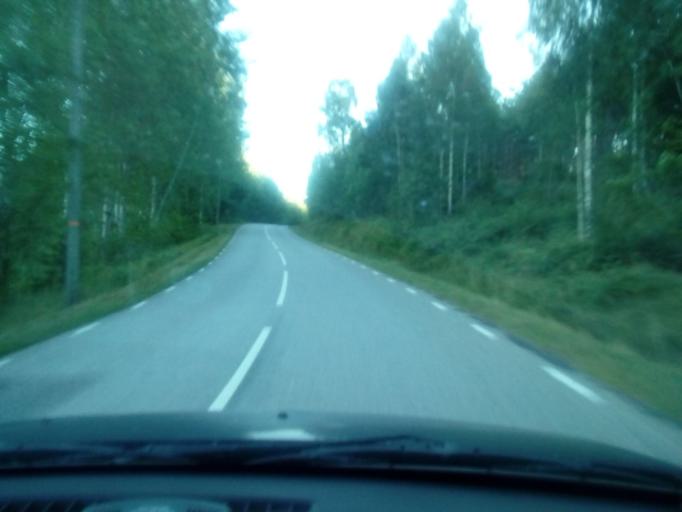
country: SE
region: Kalmar
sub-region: Vasterviks Kommun
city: Gamleby
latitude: 57.8115
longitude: 16.4354
